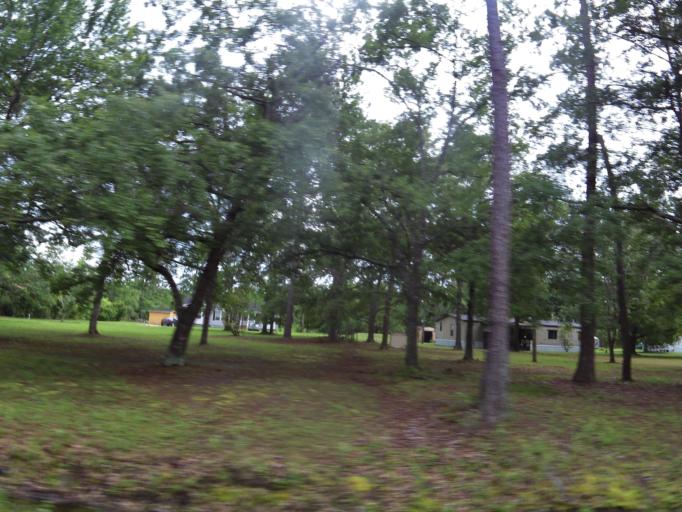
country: US
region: Florida
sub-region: Nassau County
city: Yulee
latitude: 30.5472
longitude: -81.6914
